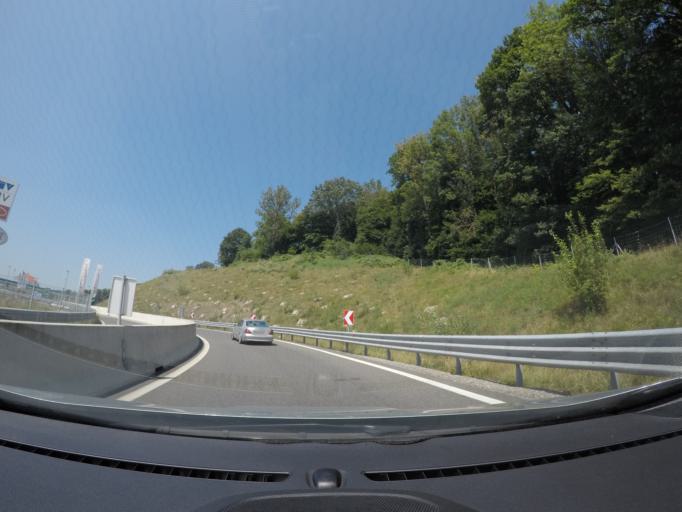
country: AT
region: Lower Austria
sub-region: Politischer Bezirk Sankt Polten
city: Altlengbach
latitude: 48.1581
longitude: 15.9441
